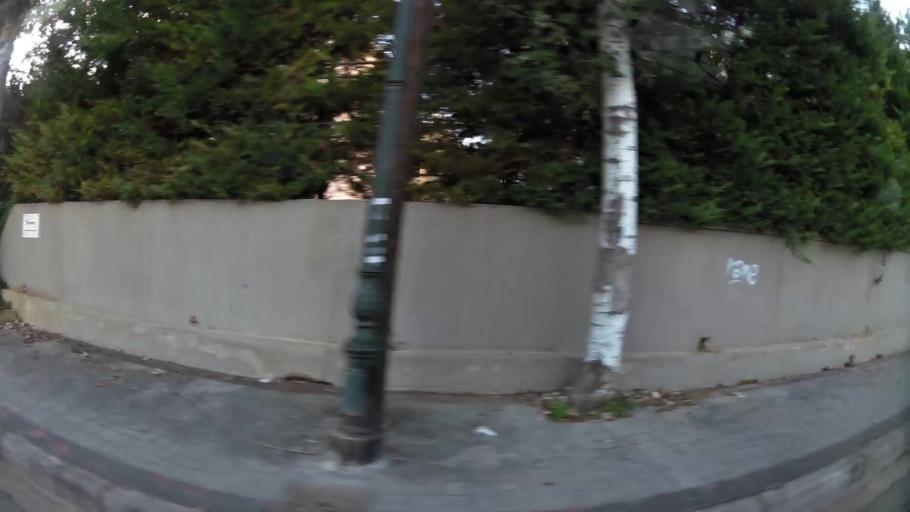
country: GR
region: Attica
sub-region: Nomarchia Anatolikis Attikis
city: Kryoneri
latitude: 38.1414
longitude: 23.8322
